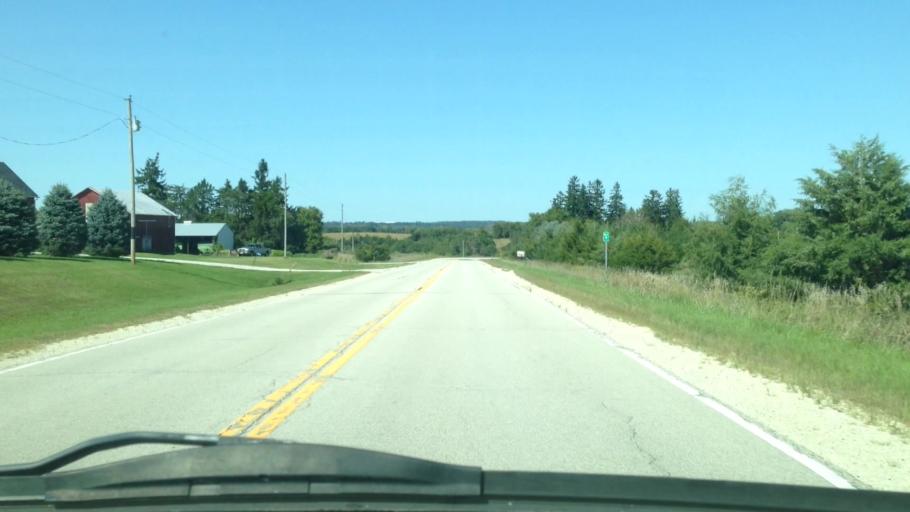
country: US
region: Minnesota
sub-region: Houston County
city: Spring Grove
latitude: 43.6388
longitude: -91.7903
